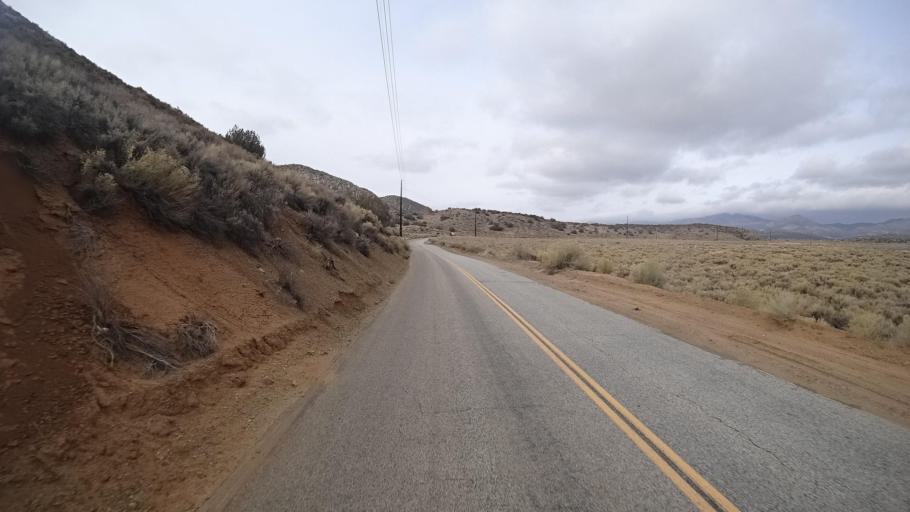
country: US
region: California
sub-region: Kern County
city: Tehachapi
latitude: 35.1523
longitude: -118.3164
